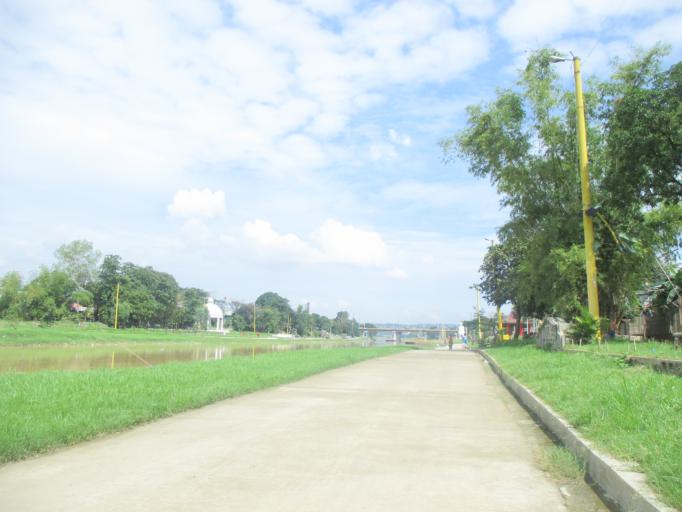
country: PH
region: Metro Manila
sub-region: Marikina
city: Calumpang
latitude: 14.6309
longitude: 121.0942
